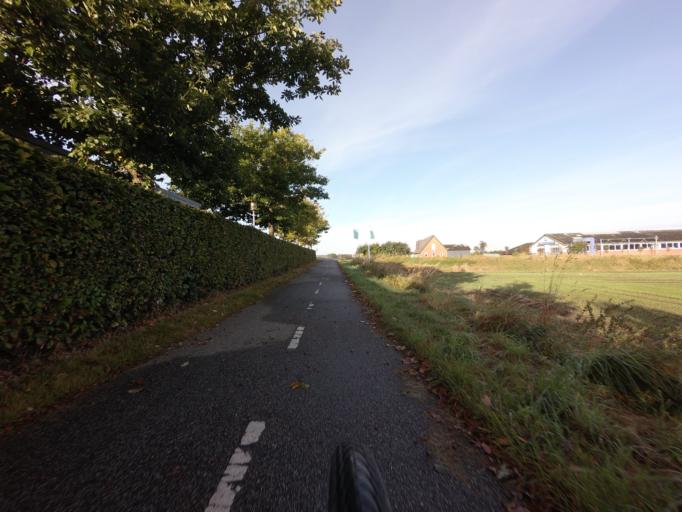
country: DK
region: Central Jutland
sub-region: Favrskov Kommune
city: Ulstrup
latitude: 56.5007
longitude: 9.7431
